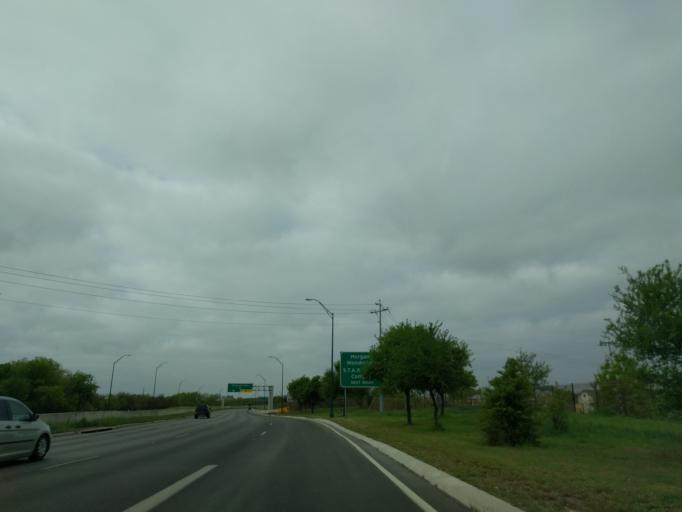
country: US
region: Texas
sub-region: Bexar County
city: Windcrest
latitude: 29.5423
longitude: -98.3890
